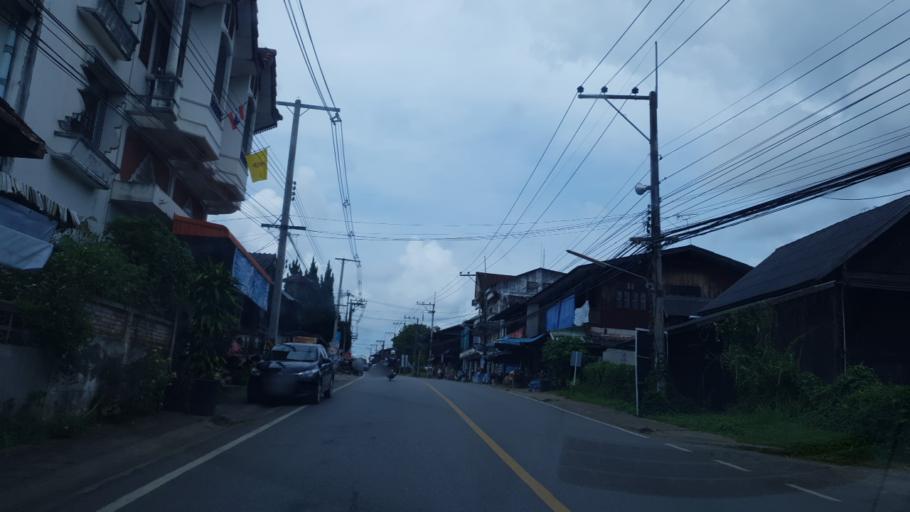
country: TH
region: Mae Hong Son
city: Khun Yuam
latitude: 18.8230
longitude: 97.9353
